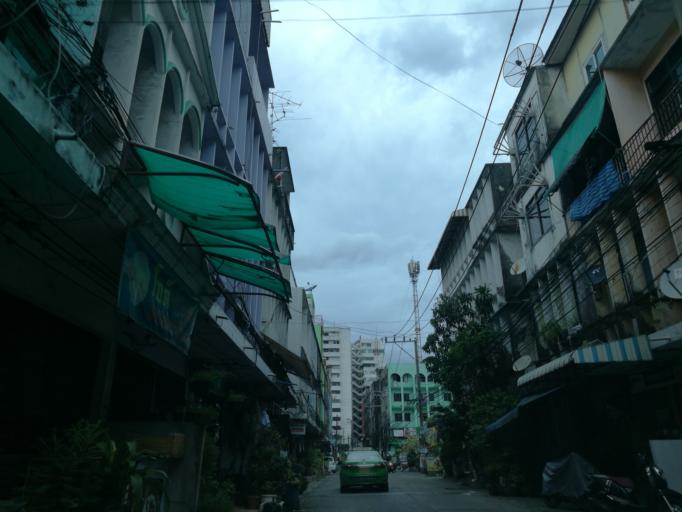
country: TH
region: Bangkok
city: Bang Sue
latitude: 13.7992
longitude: 100.5360
